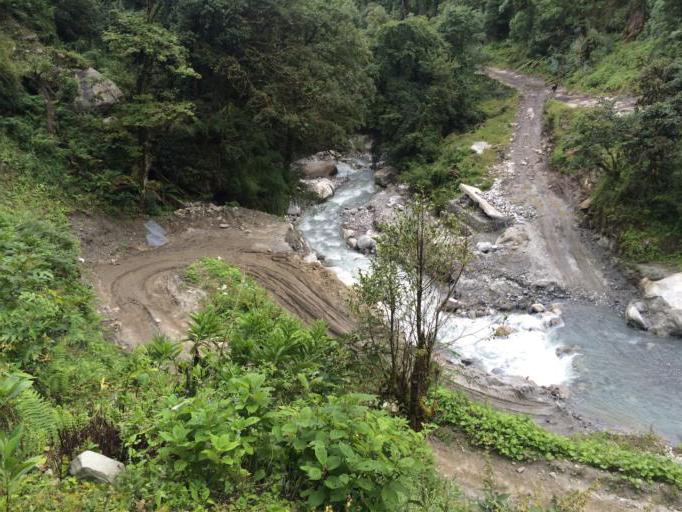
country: NP
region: Western Region
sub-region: Gandaki Zone
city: Chame
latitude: 28.5282
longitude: 84.3157
